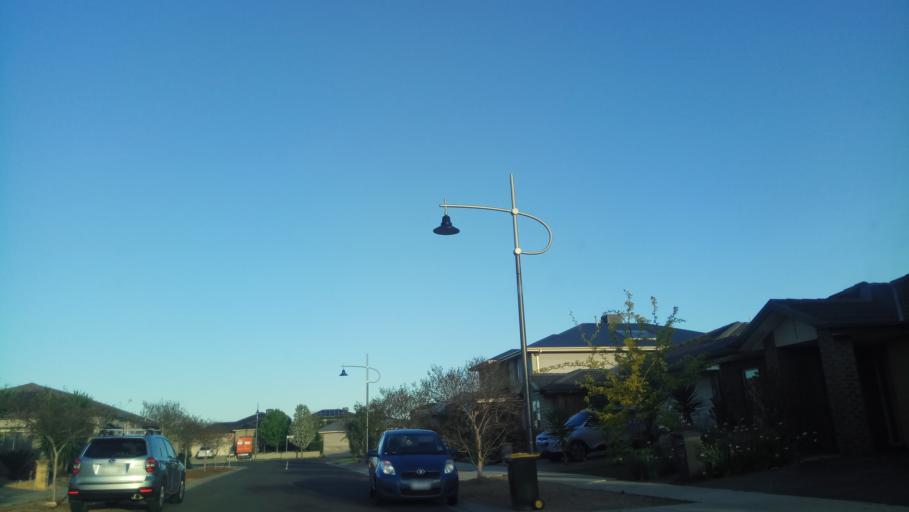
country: AU
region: Victoria
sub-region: Wyndham
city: Point Cook
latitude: -37.9062
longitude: 144.7362
